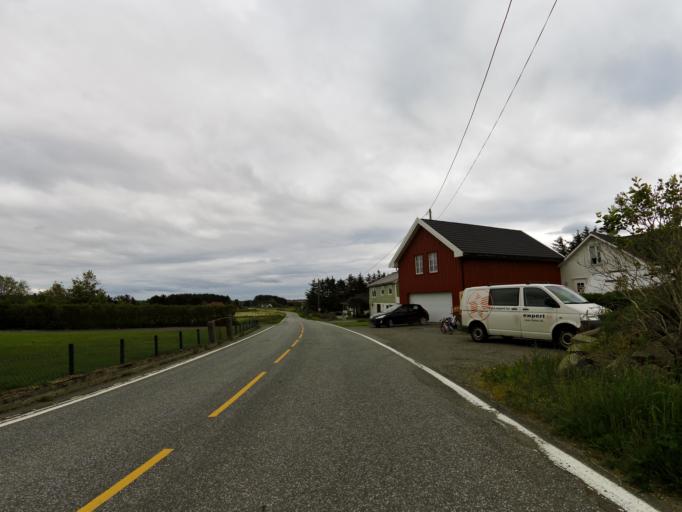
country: NO
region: Vest-Agder
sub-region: Farsund
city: Vestbygd
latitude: 58.1192
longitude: 6.6003
